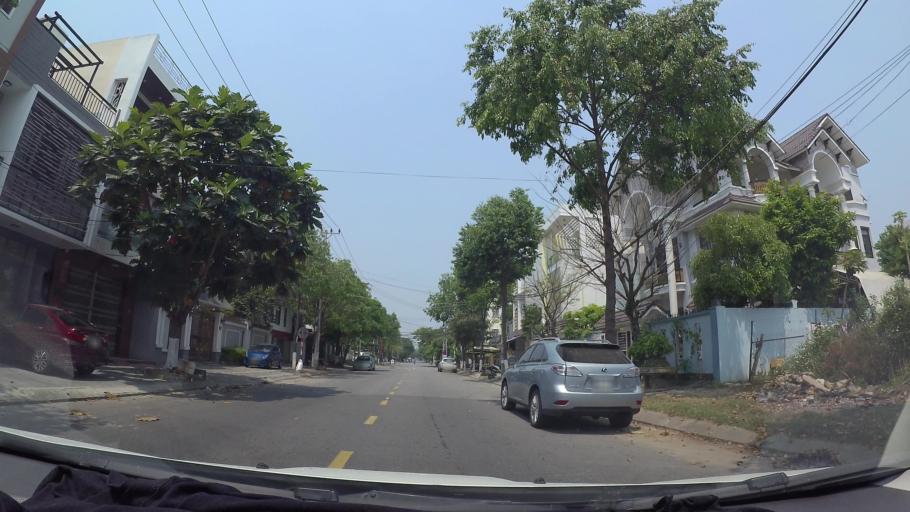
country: VN
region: Da Nang
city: Cam Le
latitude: 16.0155
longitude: 108.2096
